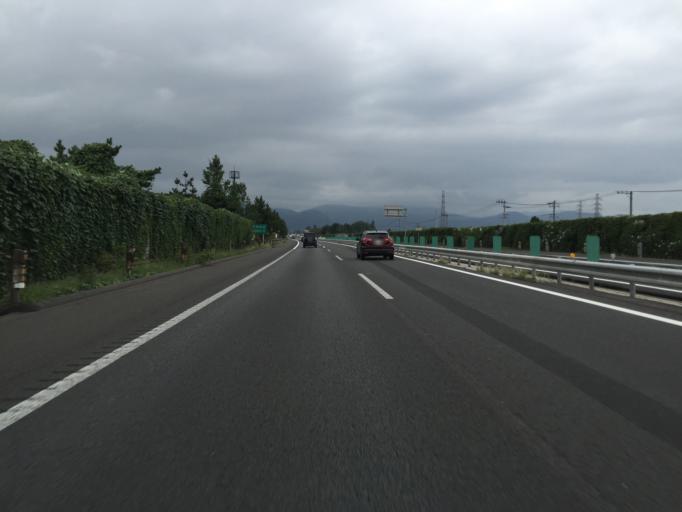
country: JP
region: Fukushima
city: Fukushima-shi
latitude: 37.7415
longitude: 140.4181
